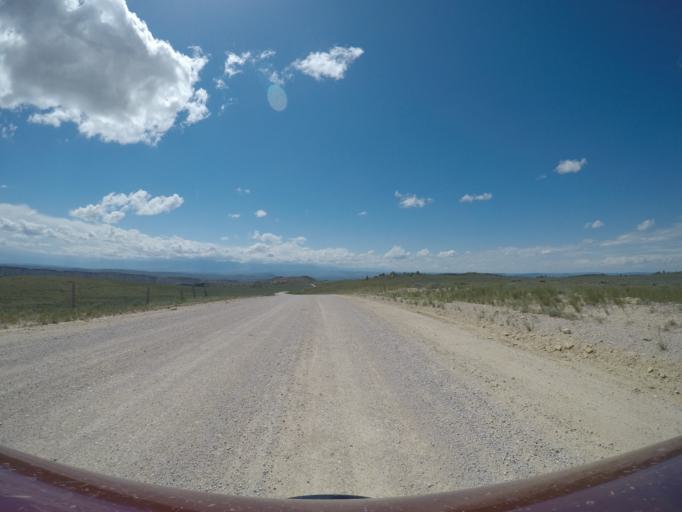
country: US
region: Wyoming
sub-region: Park County
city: Powell
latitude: 45.2066
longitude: -108.7758
